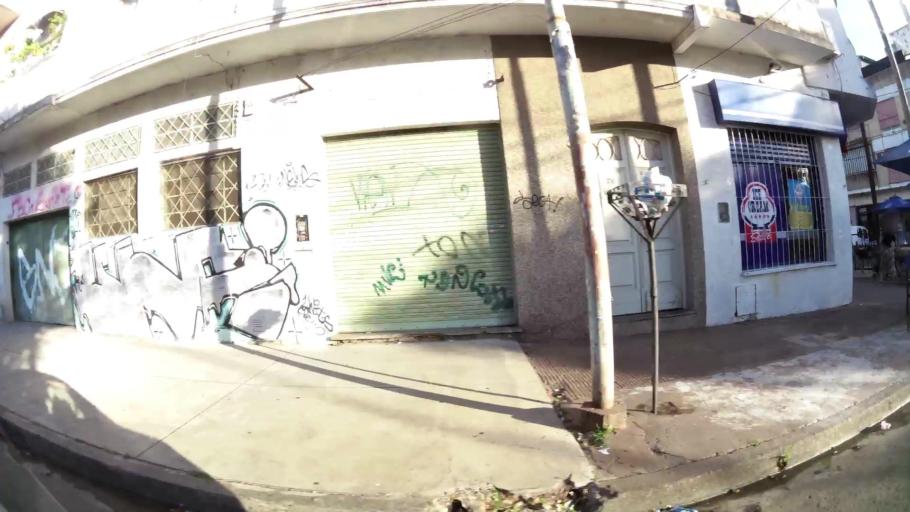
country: AR
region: Buenos Aires
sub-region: Partido de General San Martin
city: General San Martin
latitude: -34.5702
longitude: -58.5471
